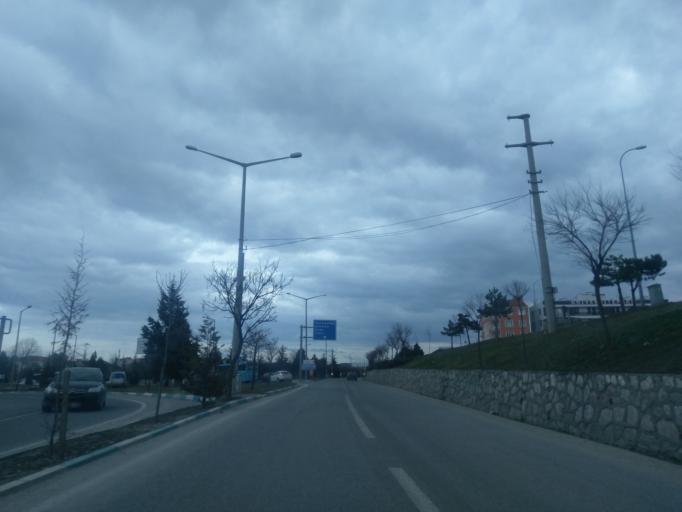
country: TR
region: Kuetahya
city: Kutahya
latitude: 39.3907
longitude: 30.0354
